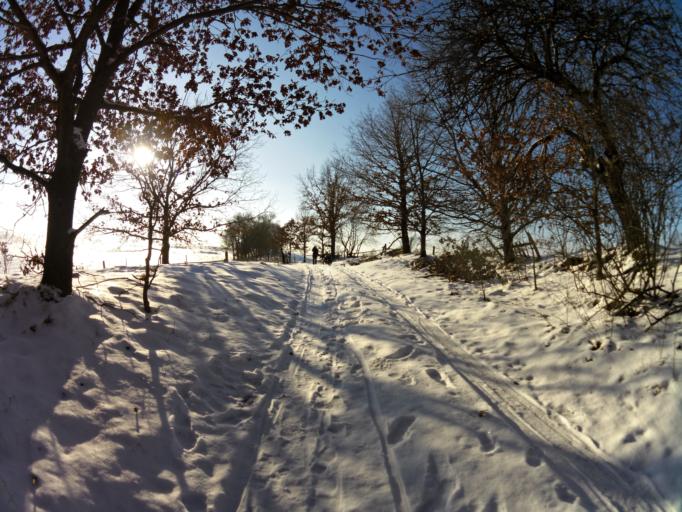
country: PL
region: West Pomeranian Voivodeship
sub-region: Powiat stargardzki
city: Dobrzany
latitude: 53.3861
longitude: 15.4868
